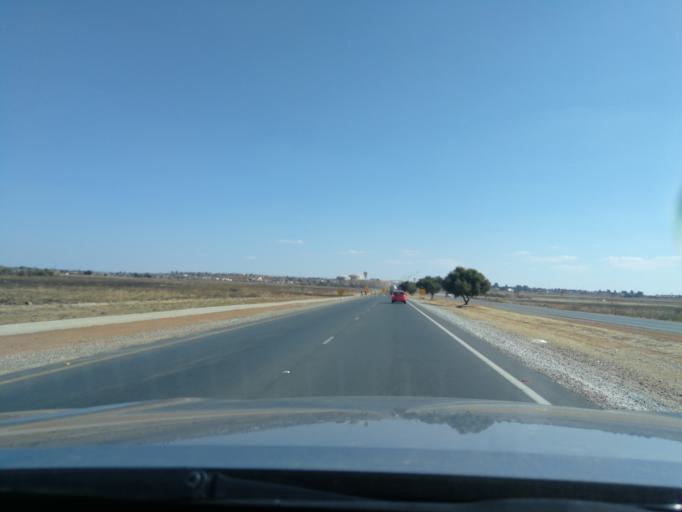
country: ZA
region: North-West
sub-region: Dr Kenneth Kaunda District Municipality
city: Klerksdorp
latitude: -26.8715
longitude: 26.6134
